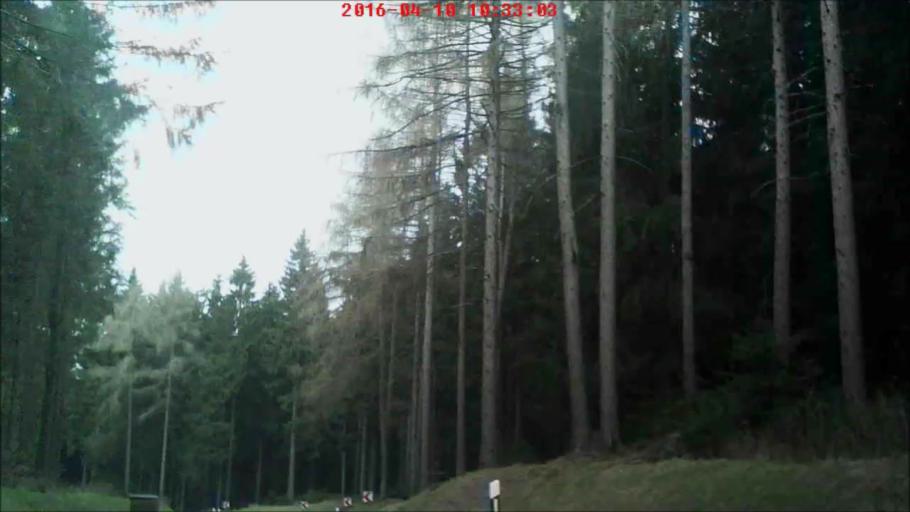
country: DE
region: Thuringia
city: Stutzerbach
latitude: 50.6070
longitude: 10.8706
